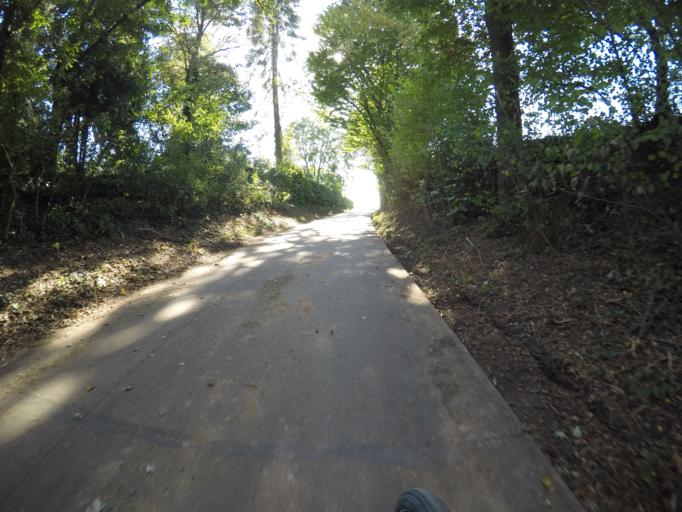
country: DE
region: Baden-Wuerttemberg
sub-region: Regierungsbezirk Stuttgart
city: Steinenbronn
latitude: 48.7004
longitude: 9.1254
